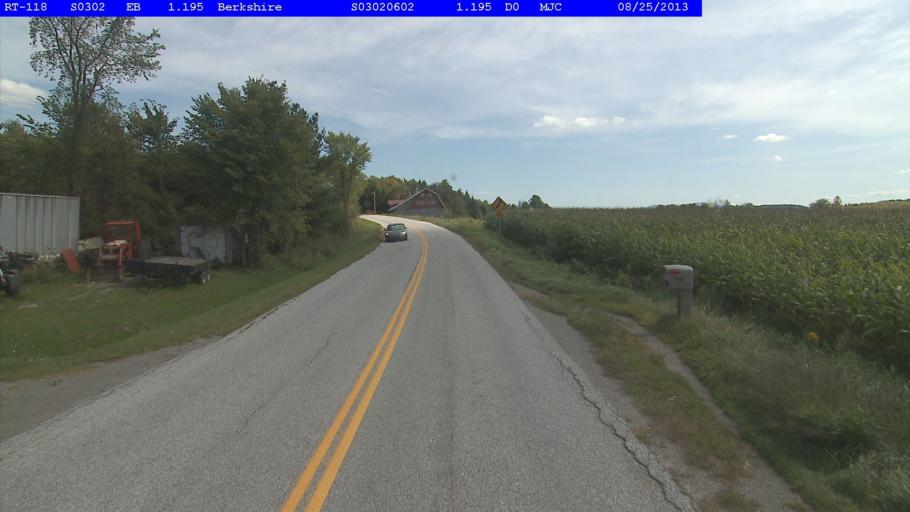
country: US
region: Vermont
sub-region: Franklin County
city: Enosburg Falls
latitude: 44.9820
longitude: -72.7923
